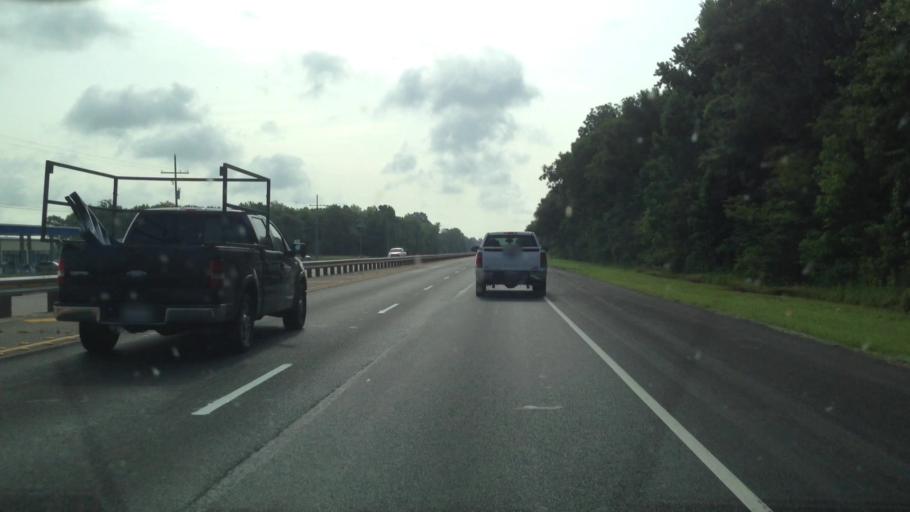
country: US
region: Louisiana
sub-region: Pointe Coupee Parish
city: Livonia
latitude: 30.5543
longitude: -91.5444
